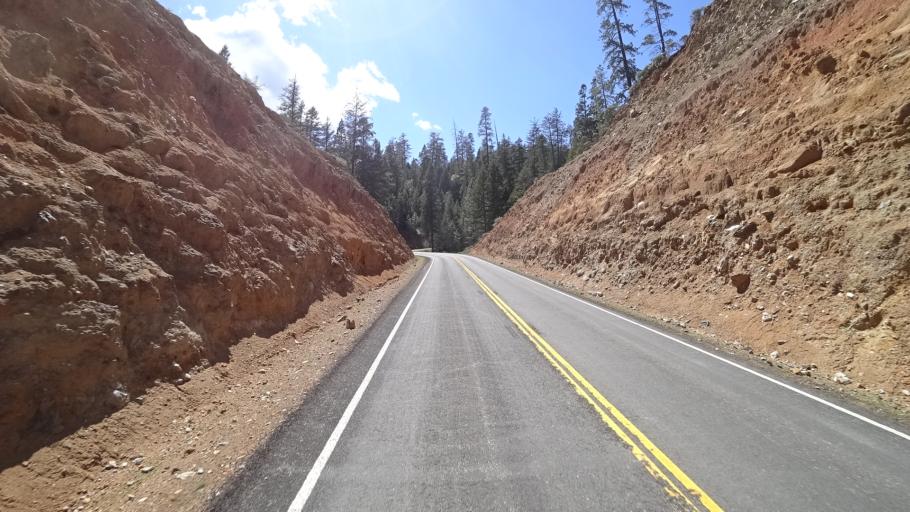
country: US
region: California
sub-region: Trinity County
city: Lewiston
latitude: 40.8529
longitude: -122.8312
